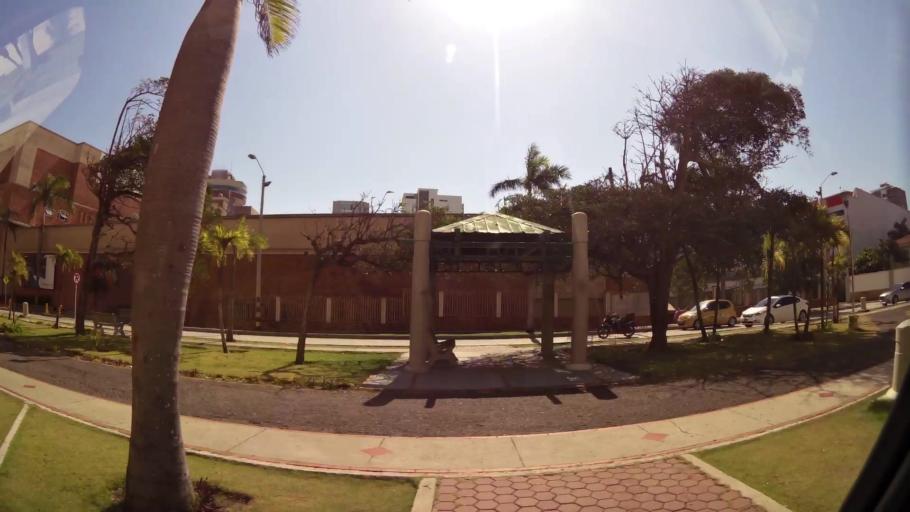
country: CO
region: Atlantico
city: Barranquilla
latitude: 11.0128
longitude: -74.8287
